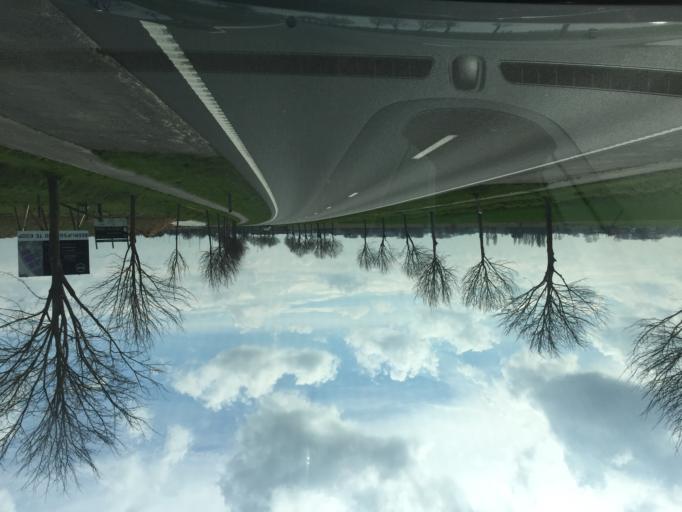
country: BE
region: Flanders
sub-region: Provincie West-Vlaanderen
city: Ruiselede
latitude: 51.0381
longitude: 3.4066
